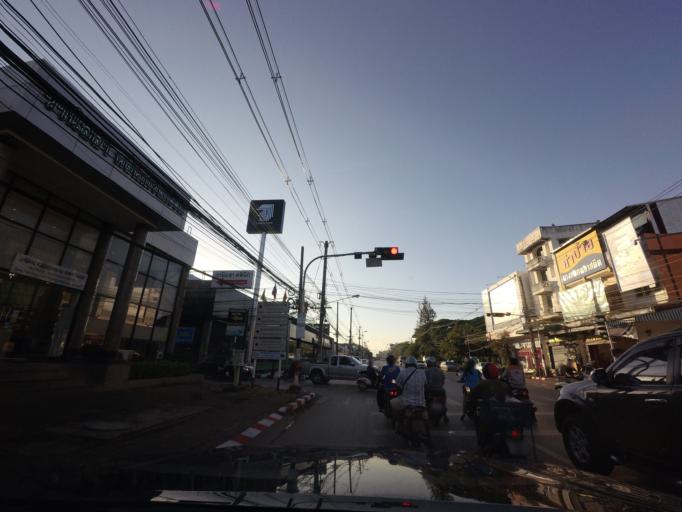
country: TH
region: Changwat Udon Thani
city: Udon Thani
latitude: 17.3999
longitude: 102.8020
